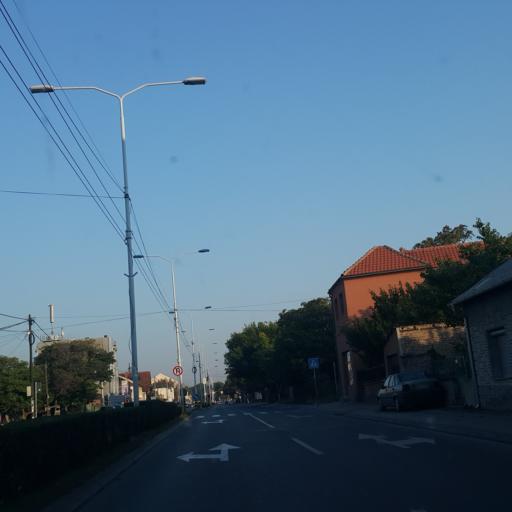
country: RS
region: Central Serbia
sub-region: Nisavski Okrug
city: Nis
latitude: 43.3268
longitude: 21.8894
